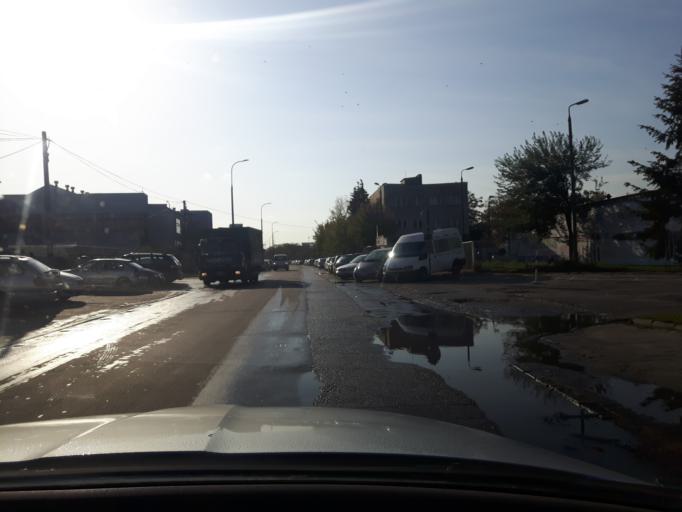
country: PL
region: Masovian Voivodeship
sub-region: Warszawa
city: Praga Polnoc
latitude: 52.2773
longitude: 21.0257
